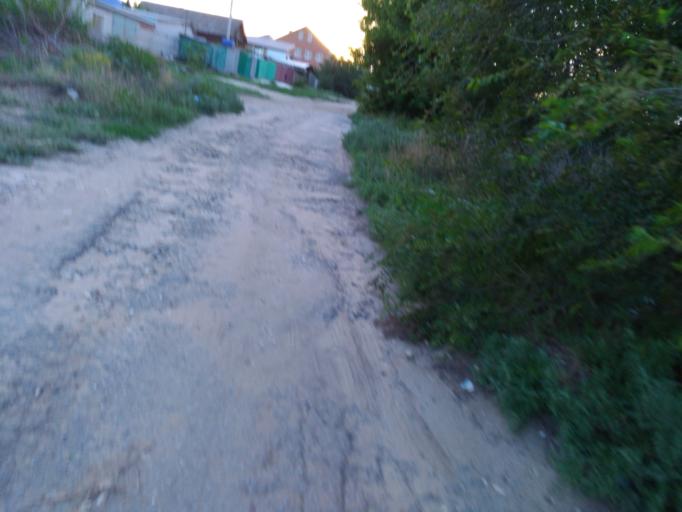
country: RU
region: Volgograd
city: Volgograd
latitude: 48.6691
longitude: 44.4534
